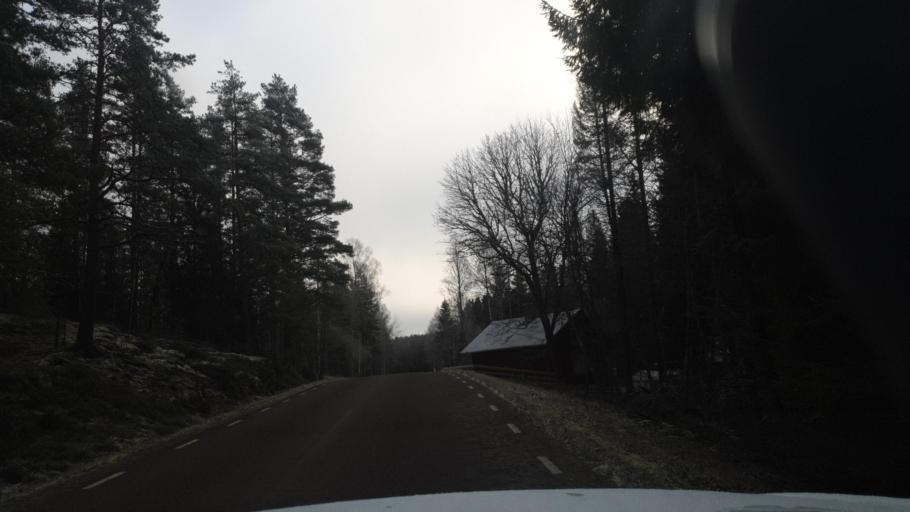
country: SE
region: Vaermland
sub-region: Karlstads Kommun
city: Valberg
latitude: 59.4531
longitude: 13.0893
